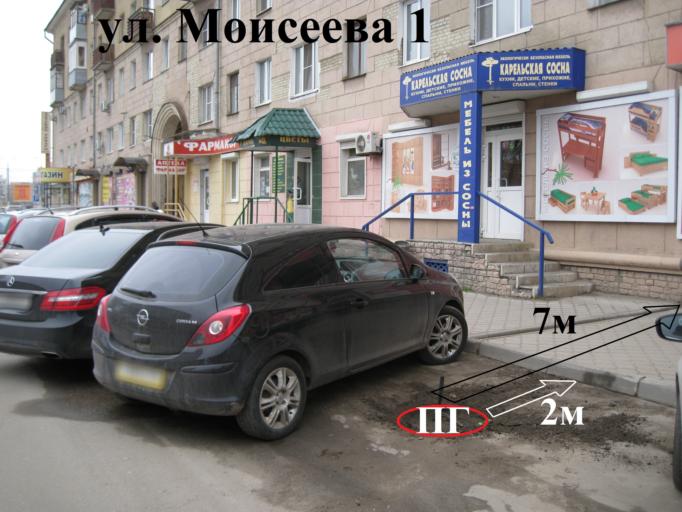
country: RU
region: Voronezj
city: Voronezh
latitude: 51.6551
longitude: 39.1855
